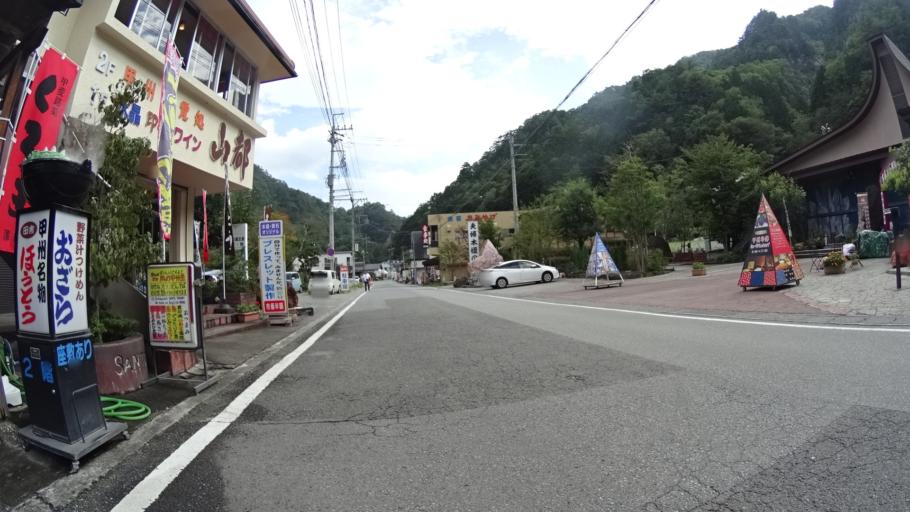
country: JP
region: Yamanashi
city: Kofu-shi
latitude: 35.7532
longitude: 138.5647
